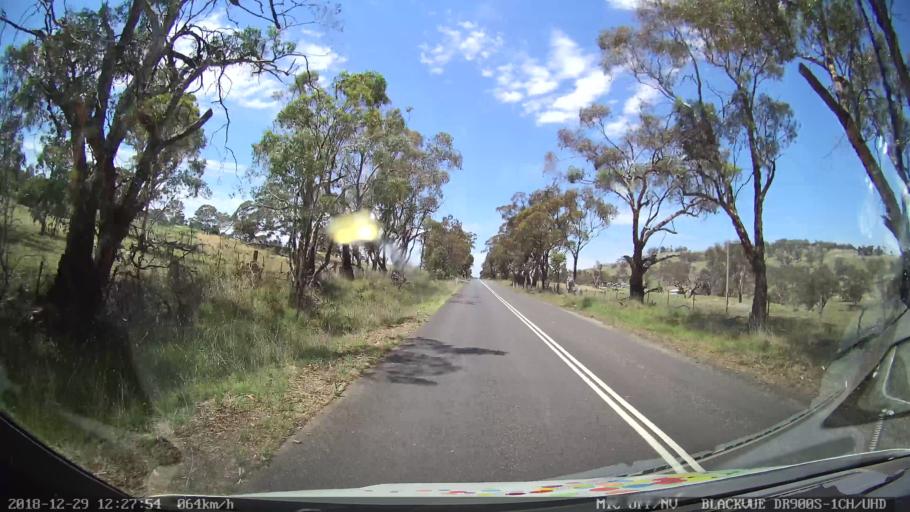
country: AU
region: Australian Capital Territory
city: Macarthur
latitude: -35.4812
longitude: 149.2246
